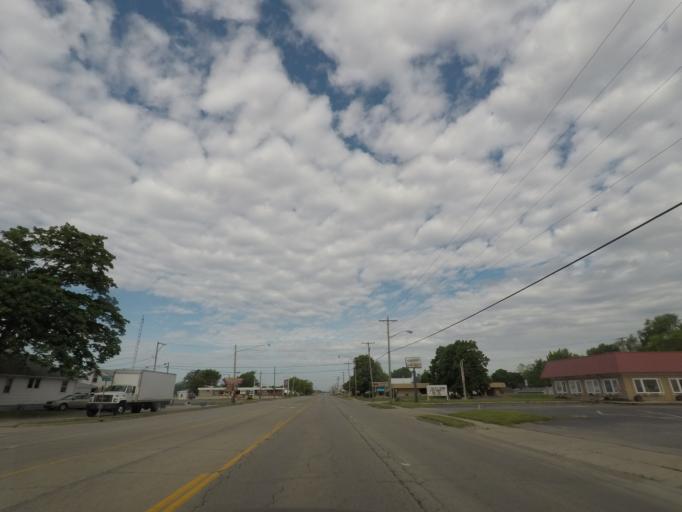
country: US
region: Illinois
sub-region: Logan County
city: Lincoln
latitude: 40.1577
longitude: -89.3789
